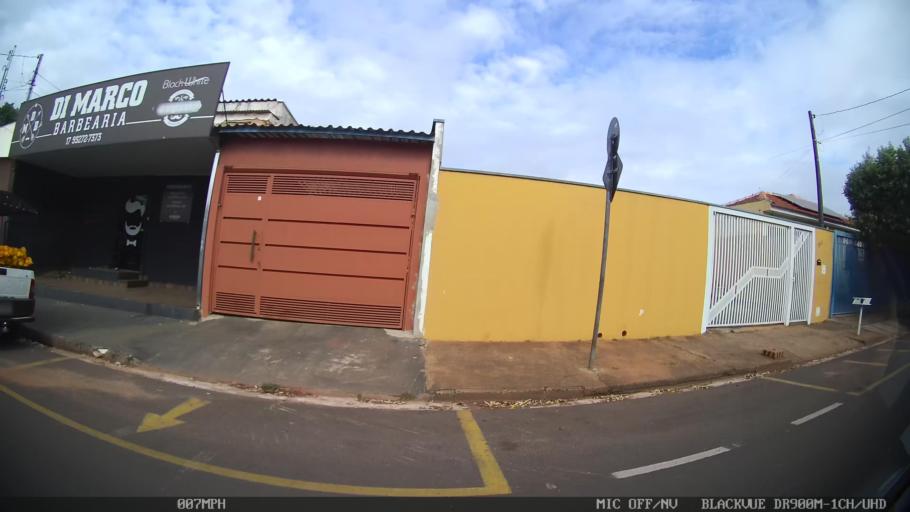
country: BR
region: Sao Paulo
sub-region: Sao Jose Do Rio Preto
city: Sao Jose do Rio Preto
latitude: -20.8226
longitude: -49.3512
